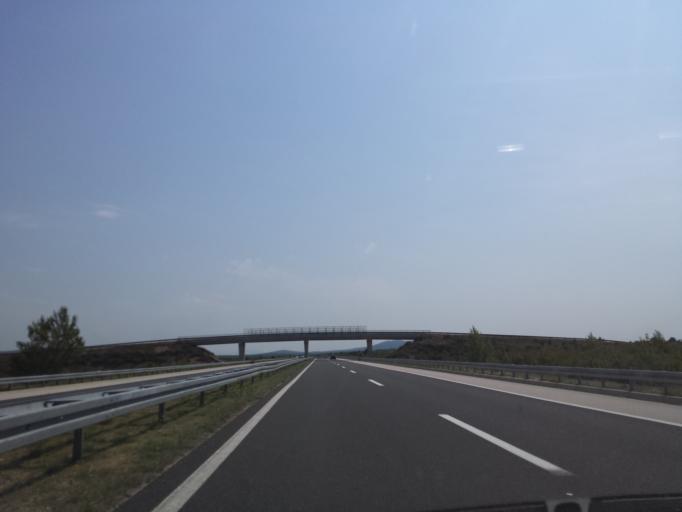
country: HR
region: Zadarska
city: Benkovac
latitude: 43.9749
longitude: 15.6432
